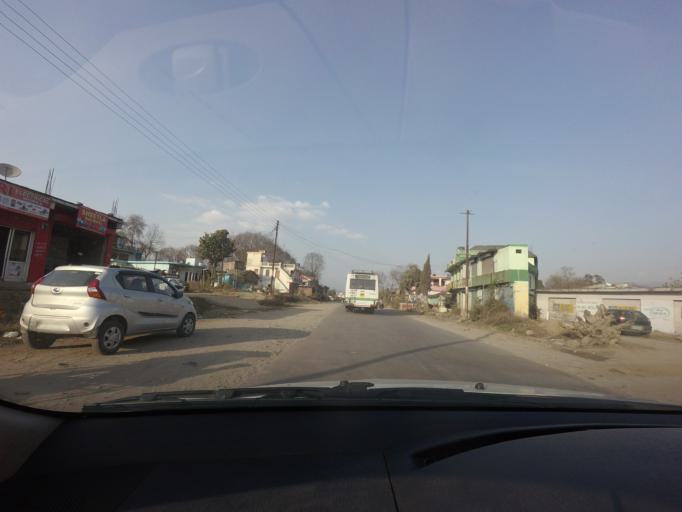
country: IN
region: Himachal Pradesh
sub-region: Mandi
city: Sundarnagar
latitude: 31.5616
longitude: 76.9037
